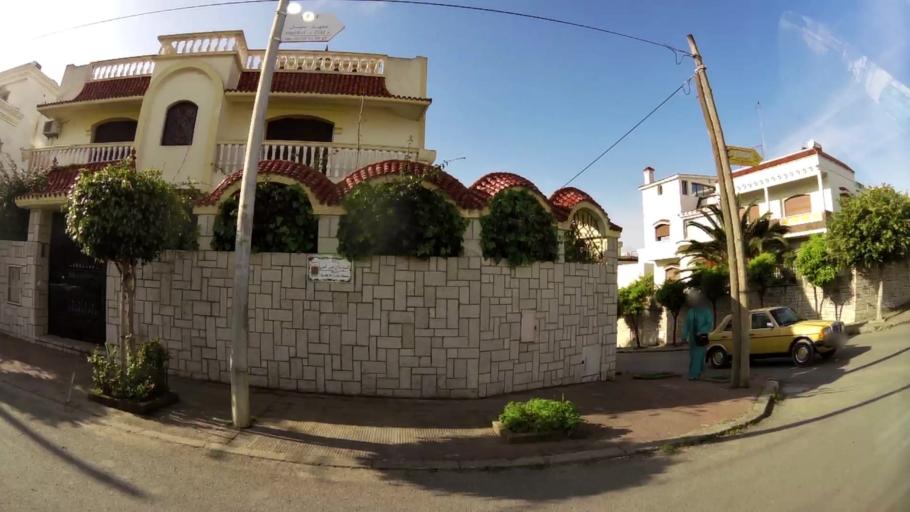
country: MA
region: Tanger-Tetouan
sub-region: Tanger-Assilah
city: Tangier
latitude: 35.7673
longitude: -5.7950
